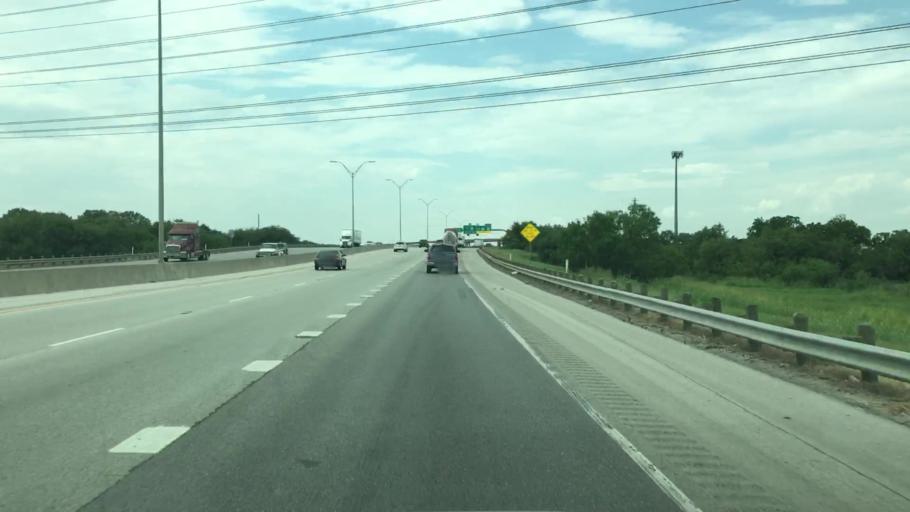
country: US
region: Texas
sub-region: Bexar County
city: China Grove
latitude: 29.3229
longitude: -98.4113
